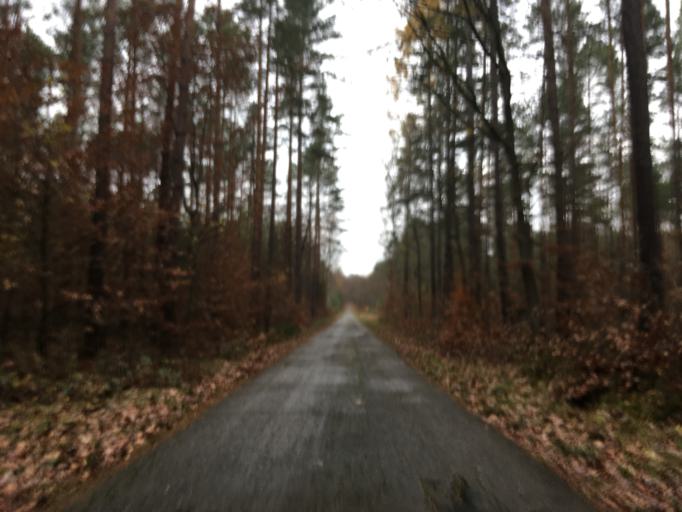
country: DE
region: Brandenburg
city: Jamlitz
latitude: 52.0776
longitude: 14.4782
